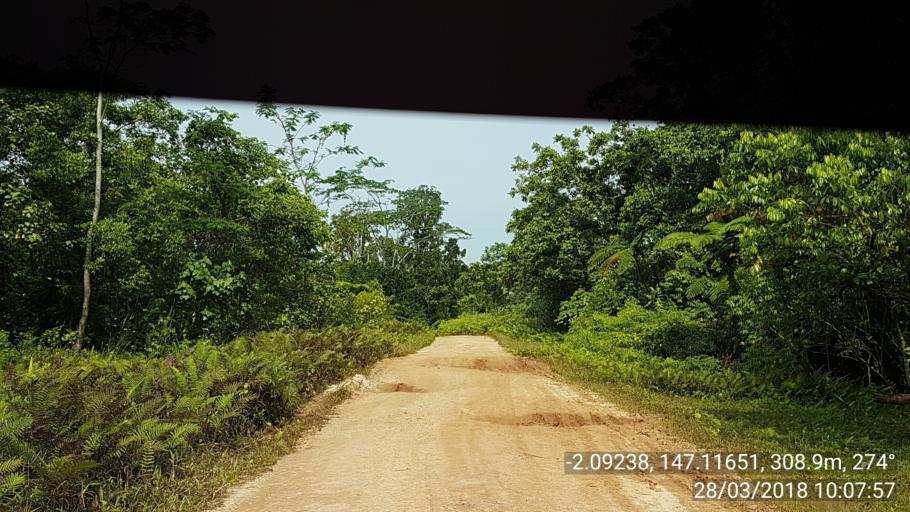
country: PG
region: Manus
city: Lorengau
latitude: -2.0925
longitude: 147.1165
